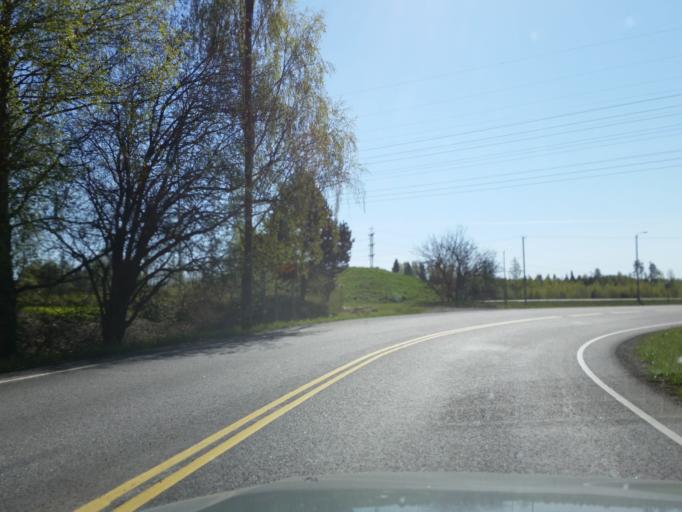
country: FI
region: Uusimaa
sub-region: Helsinki
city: Lohja
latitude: 60.1795
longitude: 23.9917
